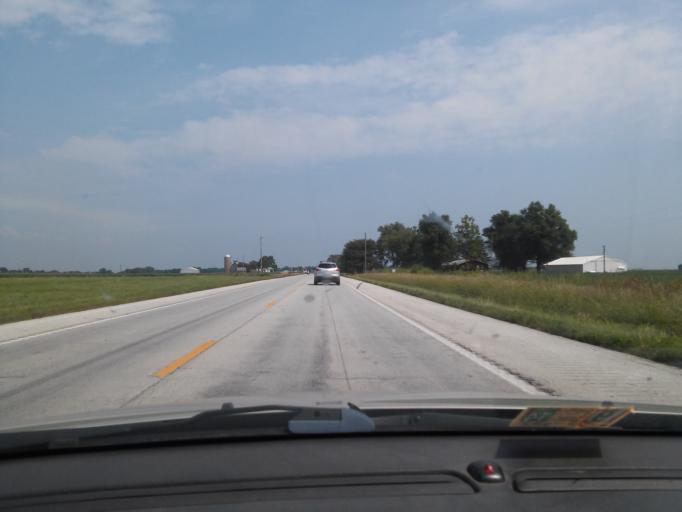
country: US
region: Missouri
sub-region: Montgomery County
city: Wellsville
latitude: 39.2169
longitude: -91.6463
